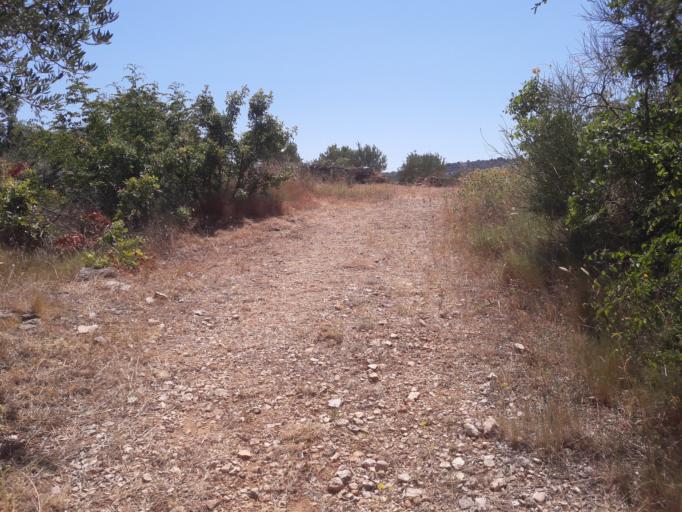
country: HR
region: Sibensko-Kniniska
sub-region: Grad Sibenik
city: Sibenik
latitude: 43.6933
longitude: 15.8539
